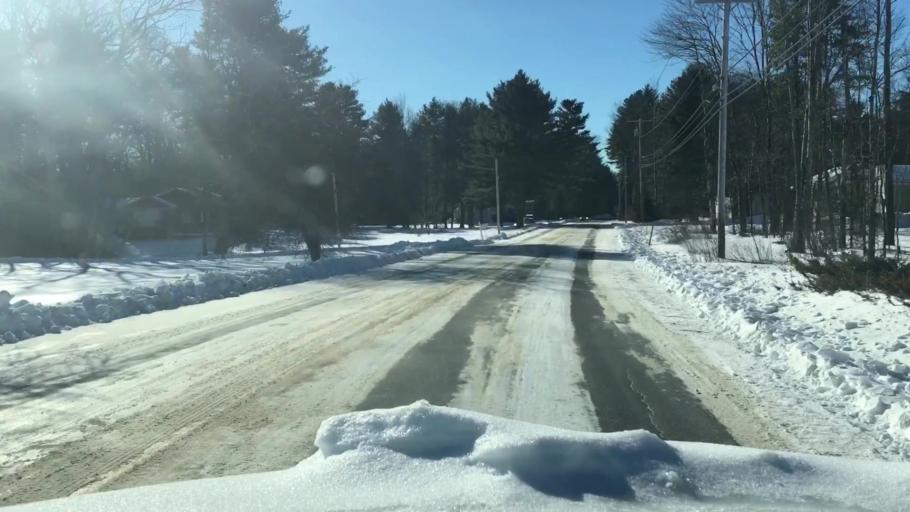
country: US
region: Maine
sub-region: Sagadahoc County
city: Topsham
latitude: 43.9565
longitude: -69.9284
